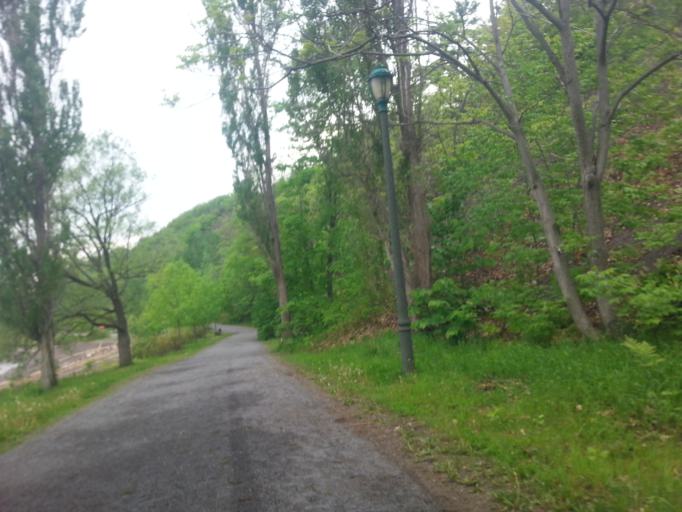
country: CA
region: Quebec
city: L'Ancienne-Lorette
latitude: 46.7492
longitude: -71.3245
